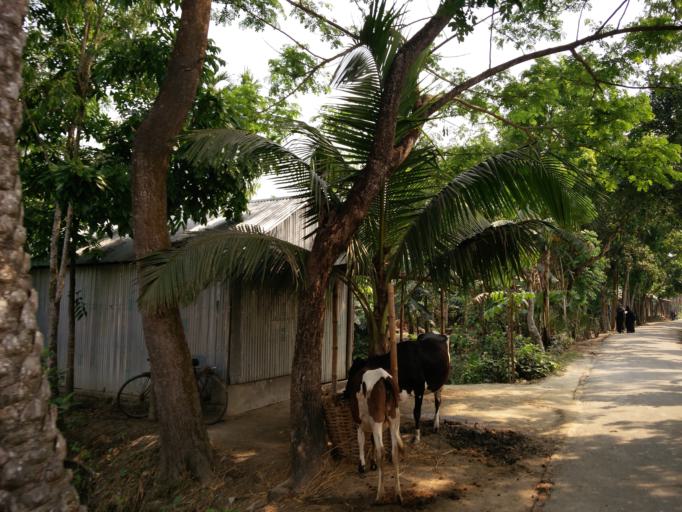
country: BD
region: Dhaka
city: Muktagacha
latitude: 24.9249
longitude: 90.2453
